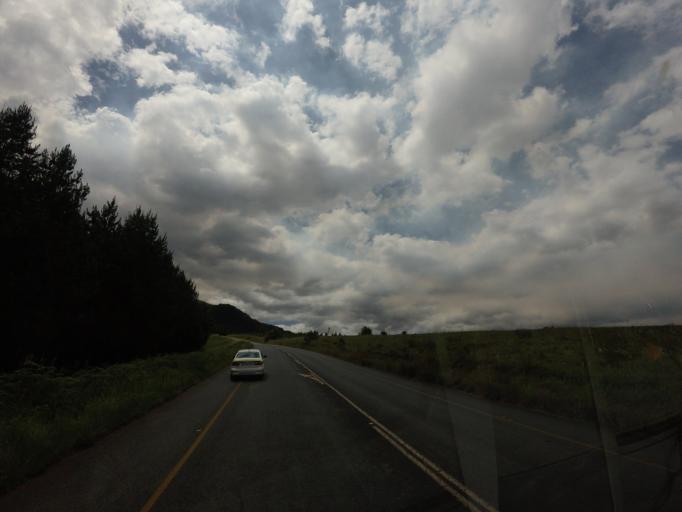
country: ZA
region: Mpumalanga
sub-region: Ehlanzeni District
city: Graksop
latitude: -24.9516
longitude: 30.8133
